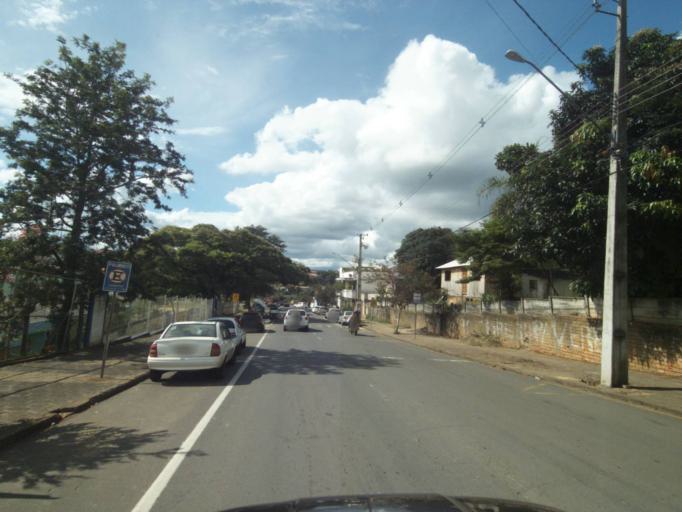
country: BR
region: Parana
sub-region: Telemaco Borba
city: Telemaco Borba
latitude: -24.3277
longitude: -50.6265
